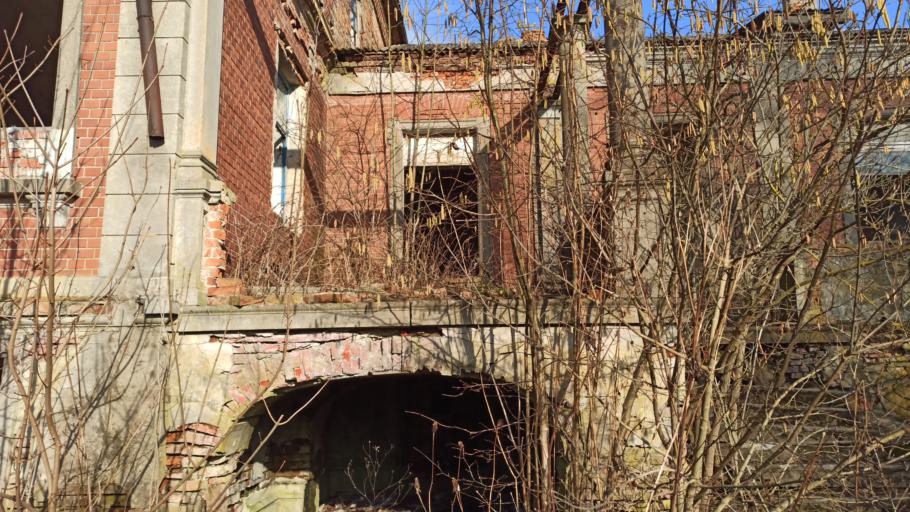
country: PL
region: Warmian-Masurian Voivodeship
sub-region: Powiat ketrzynski
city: Srokowo
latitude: 54.4690
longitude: 21.5821
